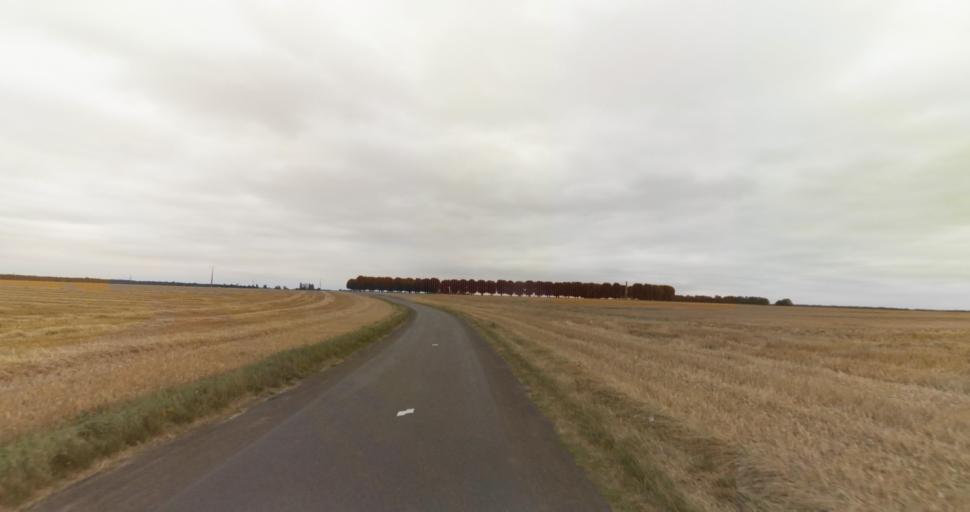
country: FR
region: Haute-Normandie
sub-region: Departement de l'Eure
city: La Couture-Boussey
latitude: 48.9252
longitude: 1.3998
